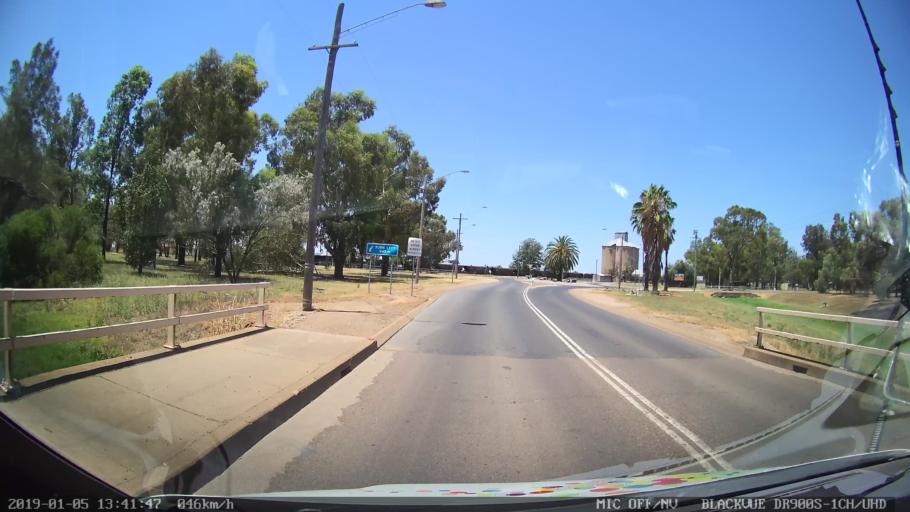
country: AU
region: New South Wales
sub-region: Gunnedah
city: Gunnedah
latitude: -30.9781
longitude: 150.2419
